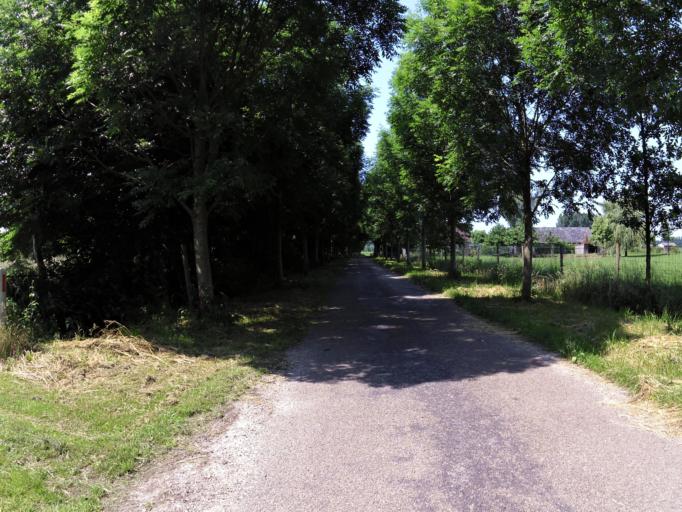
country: NL
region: North Brabant
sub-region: Gemeente Sint-Michielsgestel
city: Sint-Michielsgestel
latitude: 51.6136
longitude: 5.3478
